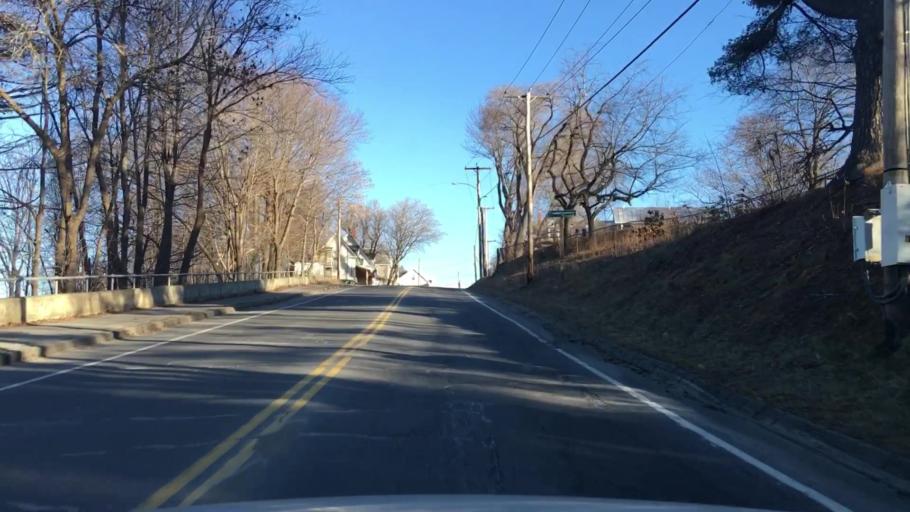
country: US
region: Maine
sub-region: Kennebec County
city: Winslow
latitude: 44.5407
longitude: -69.6259
